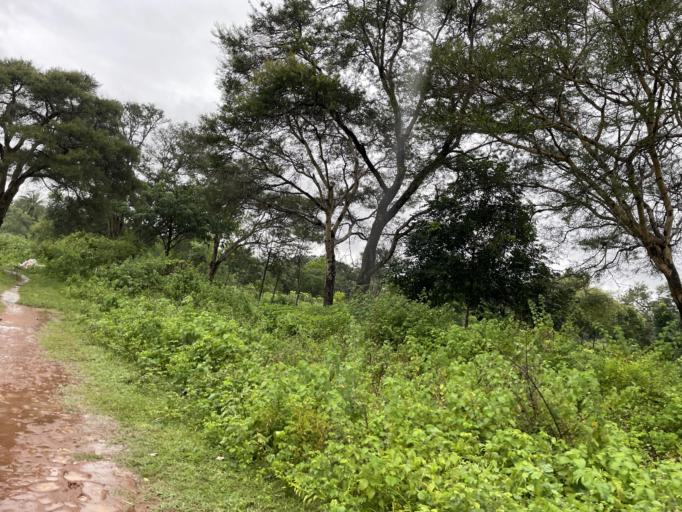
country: IN
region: Karnataka
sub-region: Bangalore Urban
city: Bangalore
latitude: 12.9422
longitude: 77.5038
